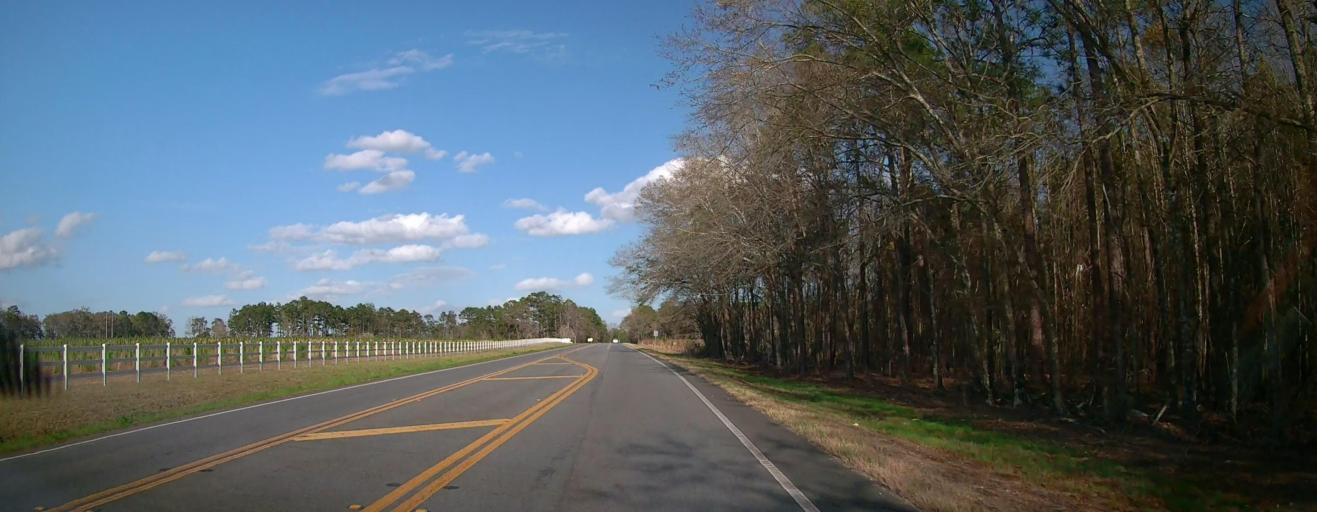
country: US
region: Georgia
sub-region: Toombs County
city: Vidalia
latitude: 32.2149
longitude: -82.4546
